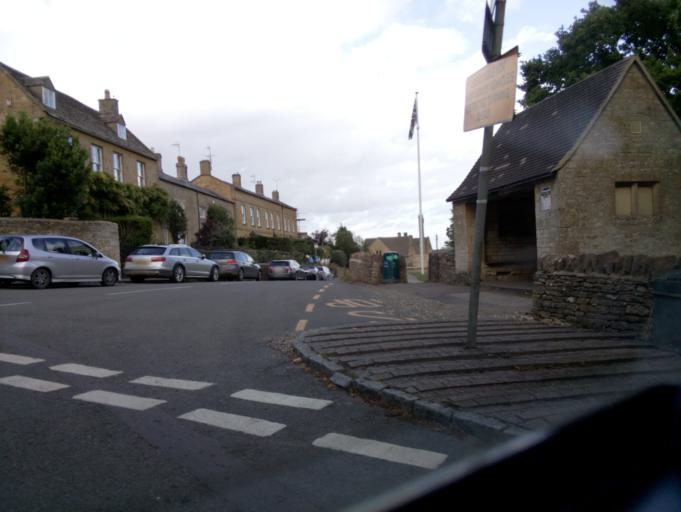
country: GB
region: England
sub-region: Gloucestershire
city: Chipping Campden
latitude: 52.0138
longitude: -1.7624
